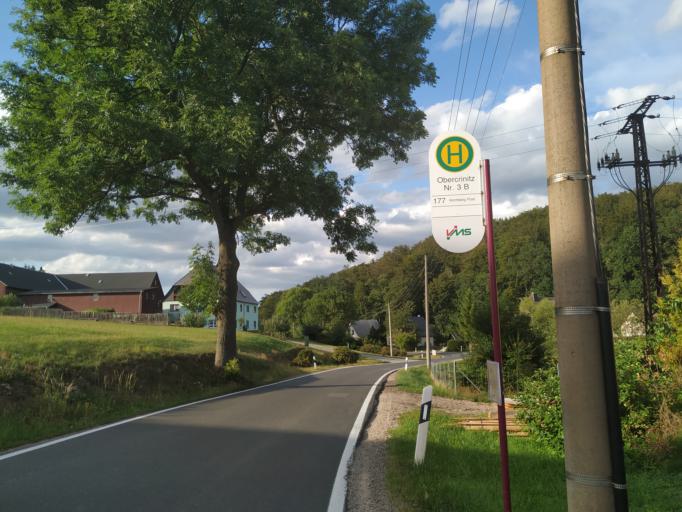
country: DE
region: Saxony
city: Kirchberg
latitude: 50.5782
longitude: 12.4920
